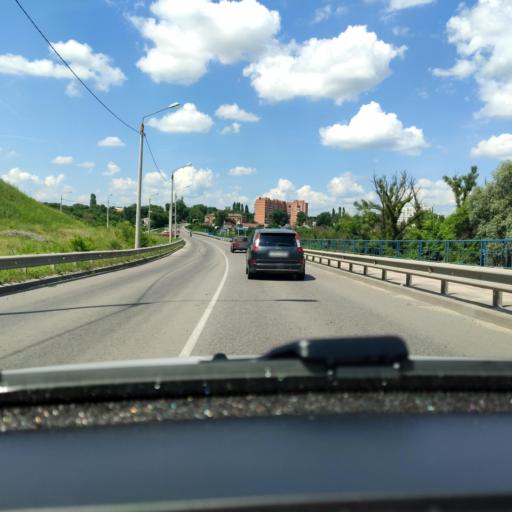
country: RU
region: Voronezj
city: Semiluki
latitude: 51.6735
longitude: 39.0338
